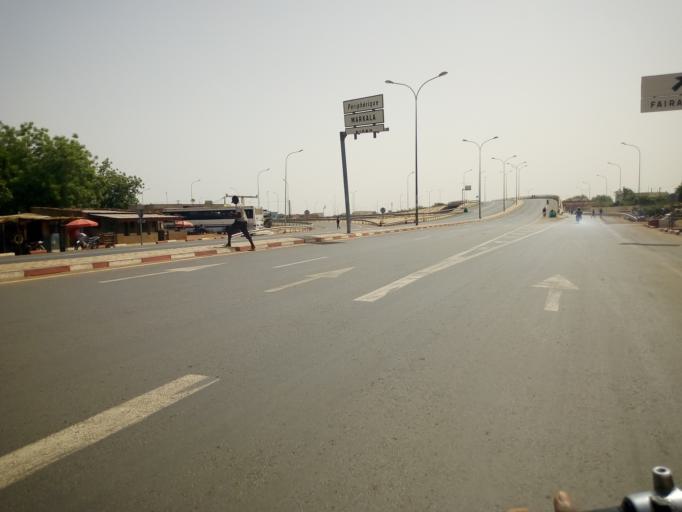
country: ML
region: Segou
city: Segou
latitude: 13.4366
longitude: -6.2409
